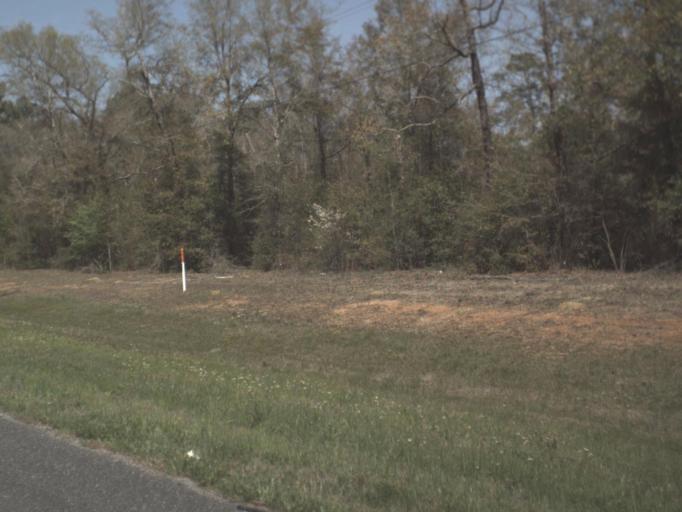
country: US
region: Florida
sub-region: Gadsden County
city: Midway
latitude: 30.5094
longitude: -84.4561
